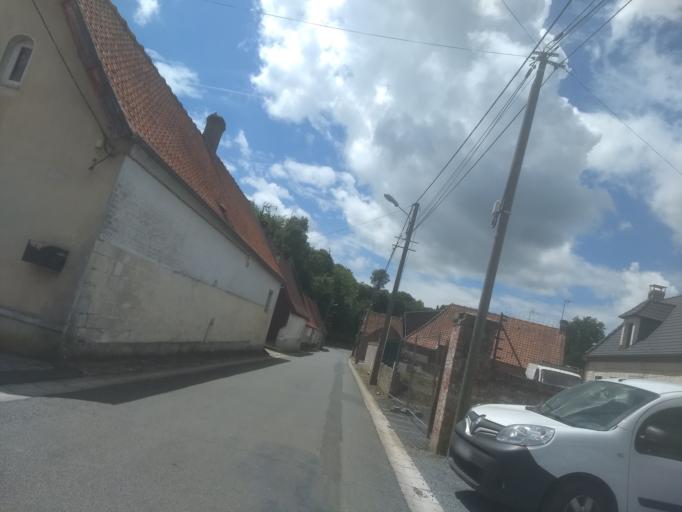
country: FR
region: Nord-Pas-de-Calais
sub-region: Departement du Pas-de-Calais
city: Riviere
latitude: 50.2387
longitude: 2.6998
